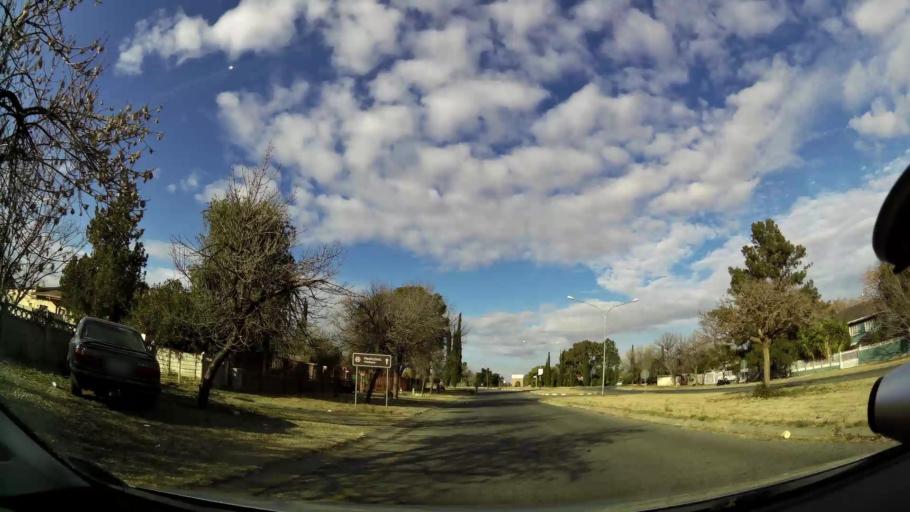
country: ZA
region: Orange Free State
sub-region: Lejweleputswa District Municipality
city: Welkom
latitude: -27.9815
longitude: 26.7103
